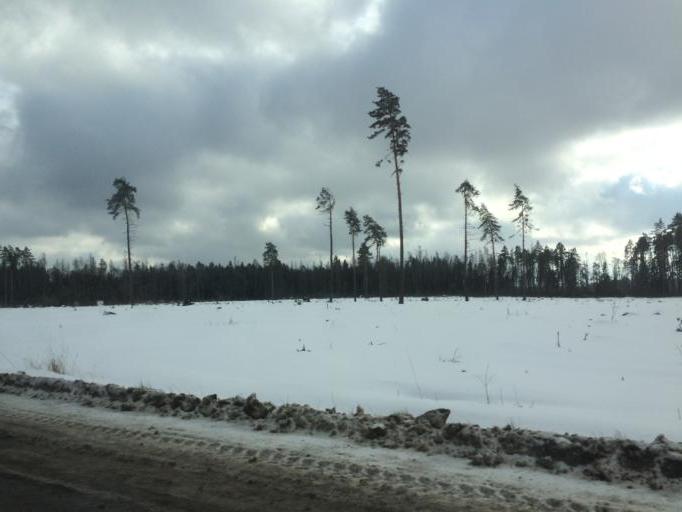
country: RU
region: Moskovskaya
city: Petrovo-Dal'neye
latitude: 55.7972
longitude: 37.1404
